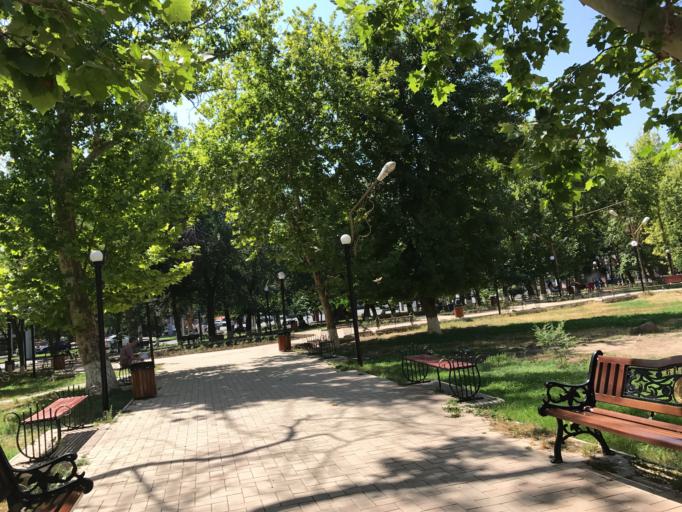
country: AM
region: Yerevan
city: Yerevan
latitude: 40.1868
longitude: 44.5165
